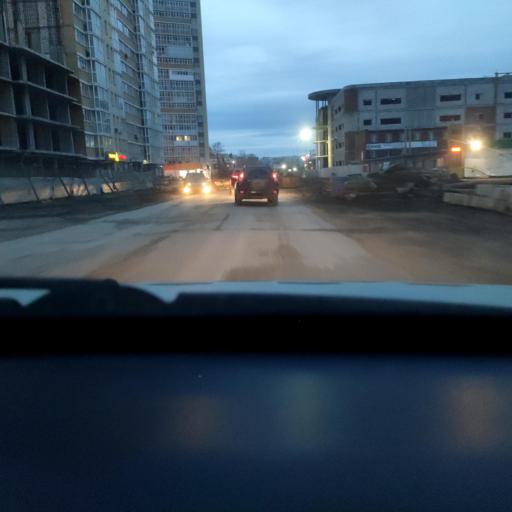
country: RU
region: Perm
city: Perm
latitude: 57.9691
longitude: 56.2035
